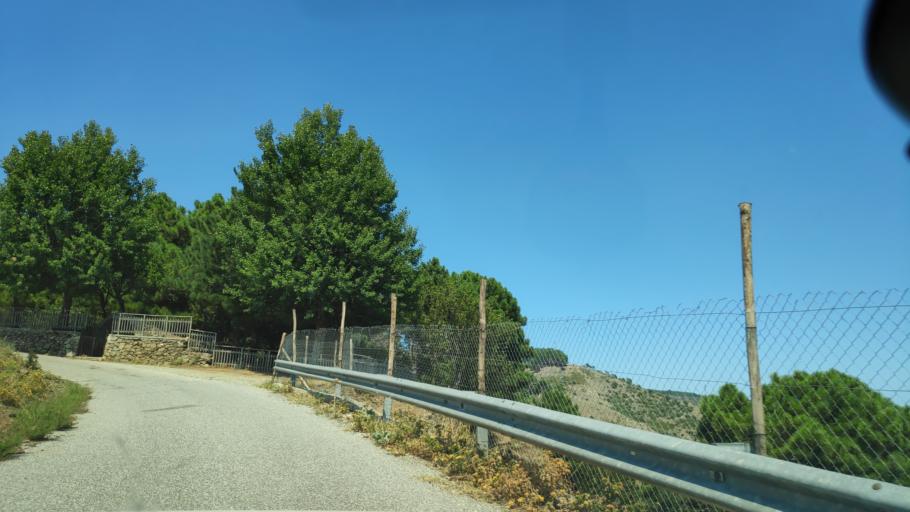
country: IT
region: Calabria
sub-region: Provincia di Reggio Calabria
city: Bova
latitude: 38.0129
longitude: 15.9354
